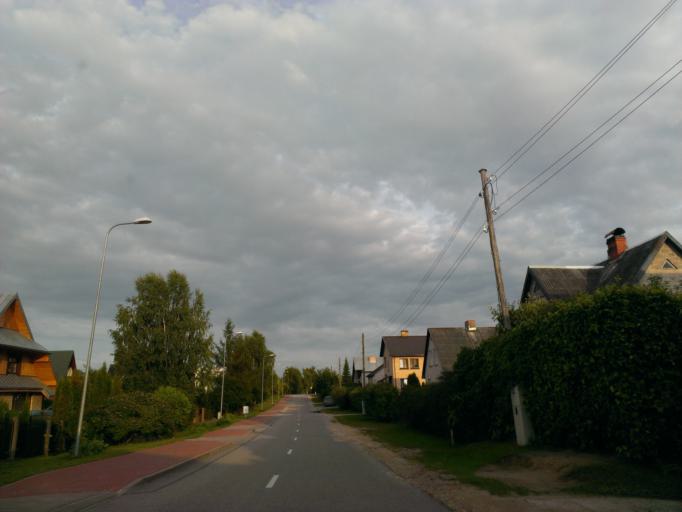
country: LV
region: Ikskile
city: Ikskile
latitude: 56.8360
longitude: 24.5116
